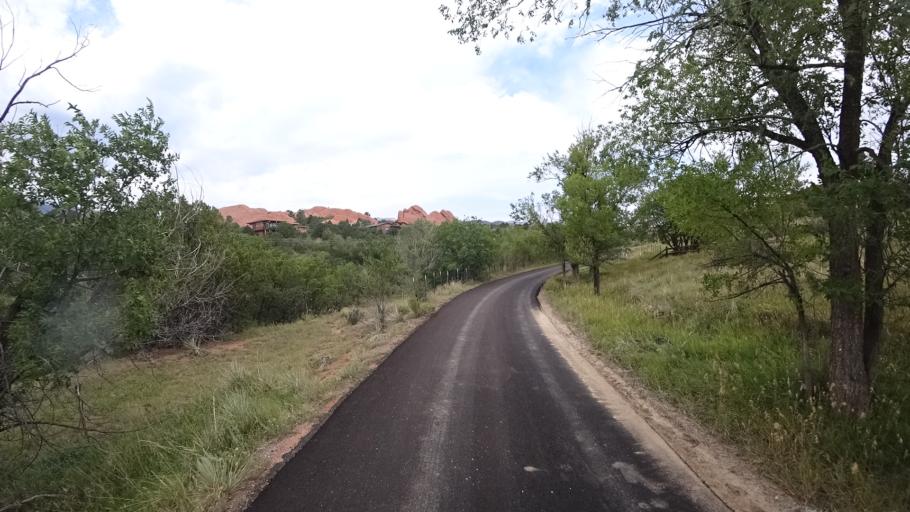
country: US
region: Colorado
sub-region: El Paso County
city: Manitou Springs
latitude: 38.8620
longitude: -104.8750
